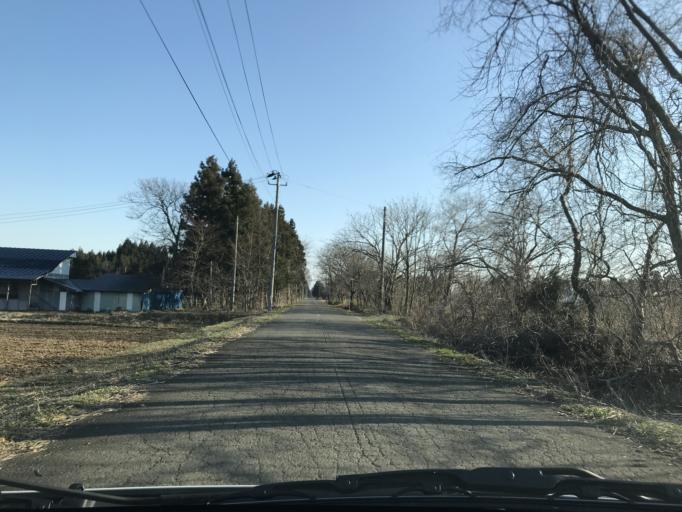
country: JP
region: Iwate
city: Kitakami
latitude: 39.2503
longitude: 141.0400
